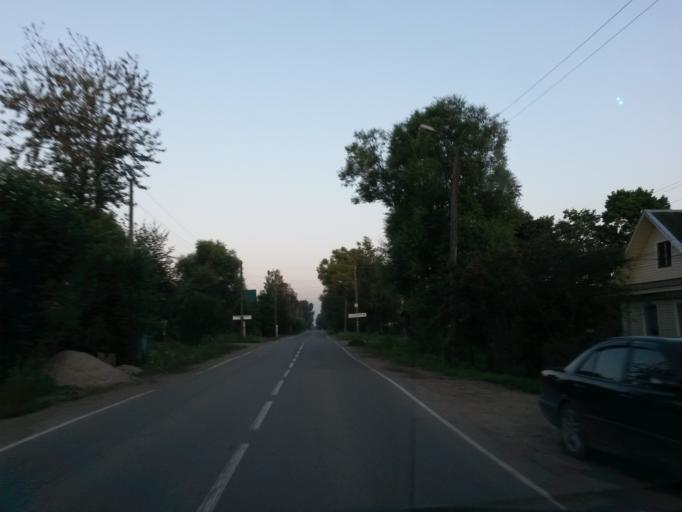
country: RU
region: Jaroslavl
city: Tutayev
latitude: 57.8903
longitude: 39.5331
